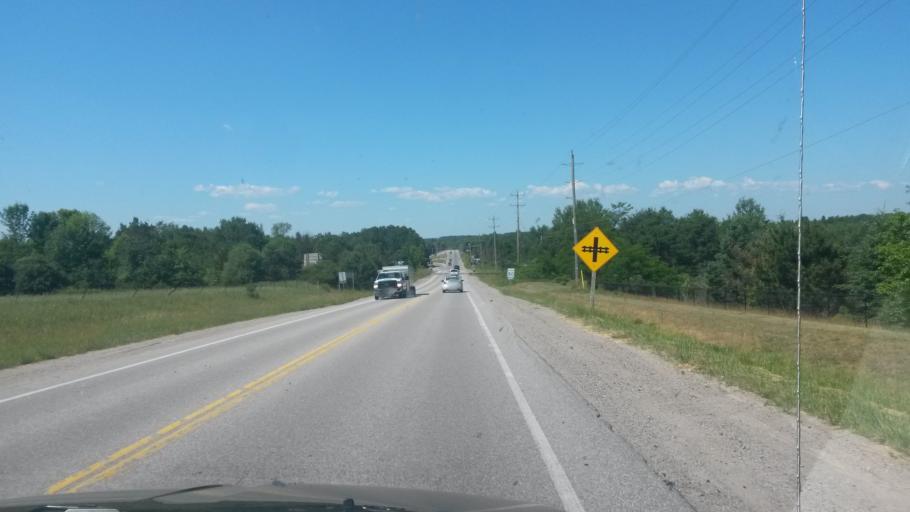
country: CA
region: Ontario
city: Barrie
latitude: 44.5270
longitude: -79.7319
